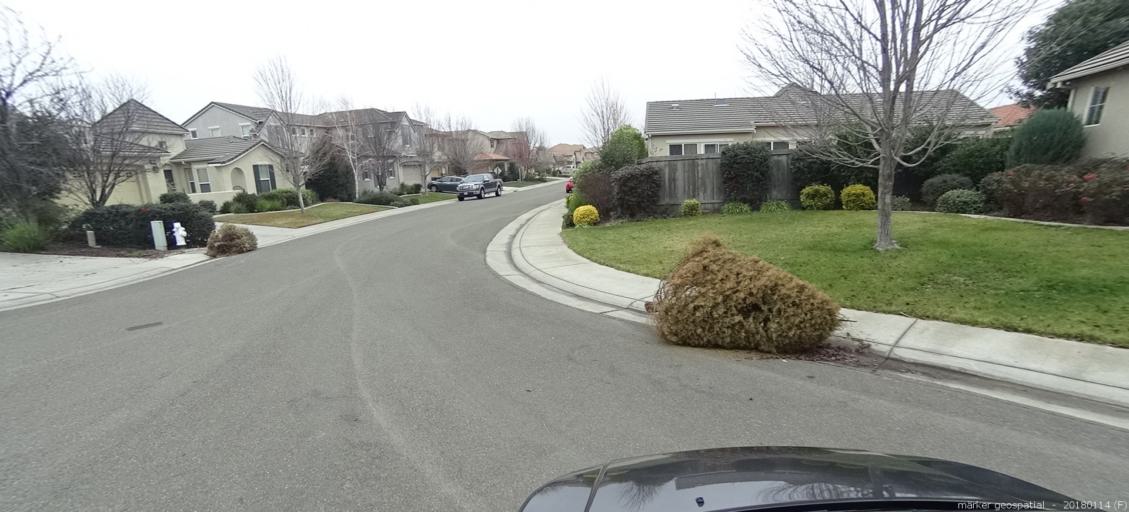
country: US
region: California
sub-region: Sacramento County
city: Rancho Cordova
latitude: 38.5402
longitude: -121.2375
